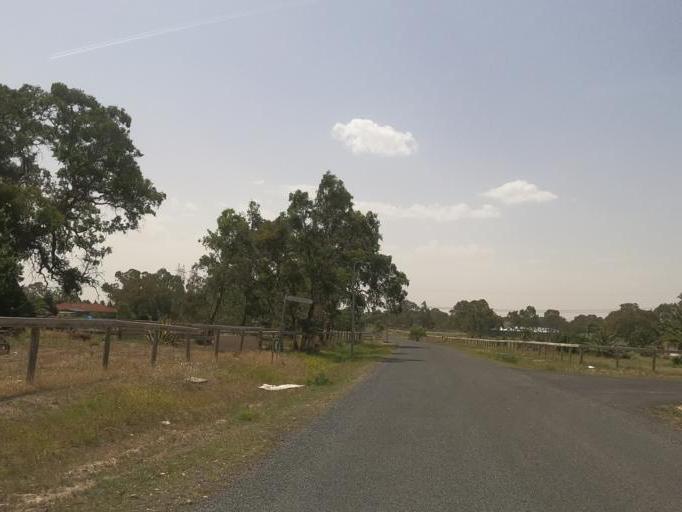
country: AU
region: Victoria
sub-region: Hume
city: Craigieburn
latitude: -37.5543
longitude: 144.8990
